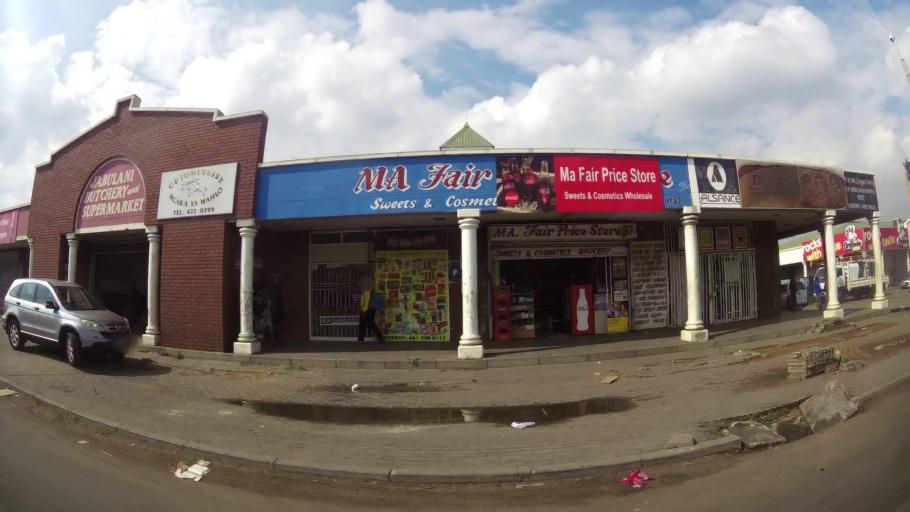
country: ZA
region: Gauteng
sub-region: Sedibeng District Municipality
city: Vereeniging
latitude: -26.6780
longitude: 27.9332
